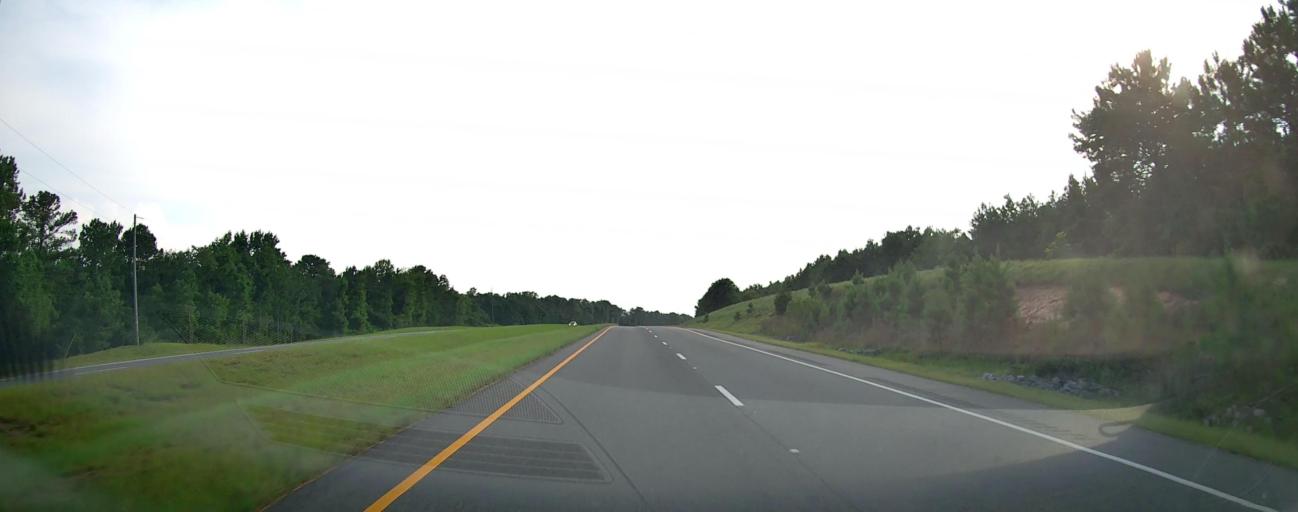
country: US
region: Georgia
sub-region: Talbot County
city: Talbotton
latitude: 32.5809
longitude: -84.5235
